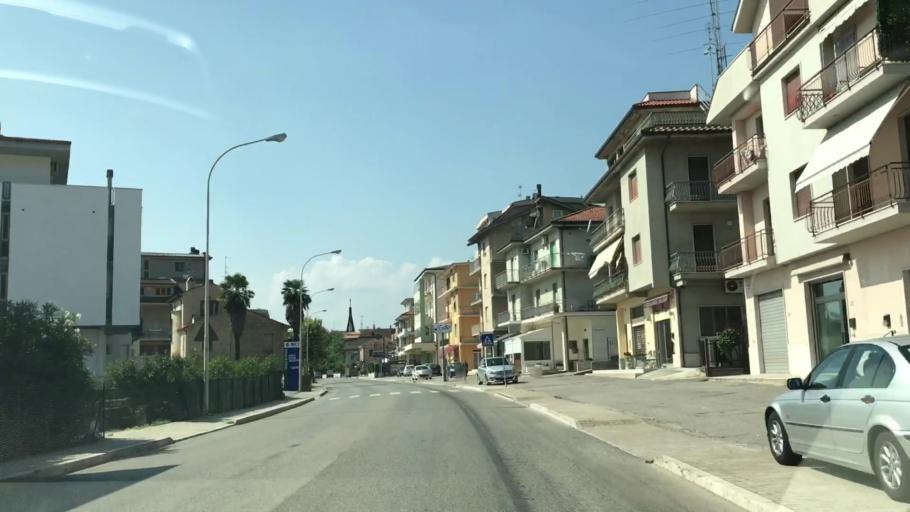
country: IT
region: The Marches
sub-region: Provincia di Ascoli Piceno
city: Stella
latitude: 42.8880
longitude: 13.8142
